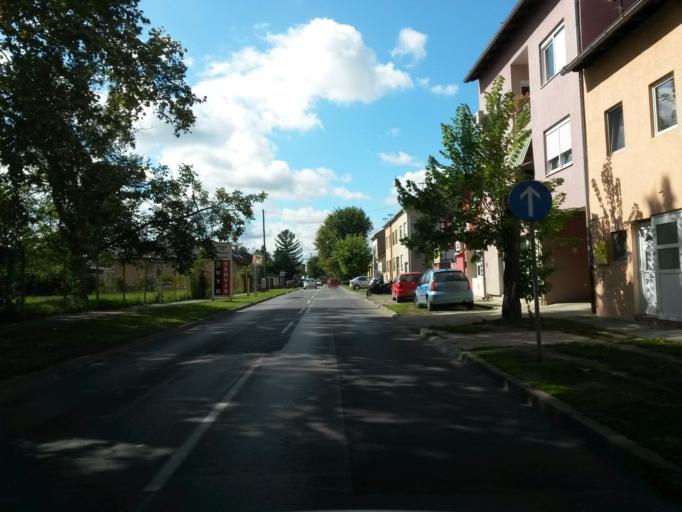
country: HR
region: Osjecko-Baranjska
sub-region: Grad Osijek
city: Osijek
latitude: 45.5571
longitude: 18.6619
